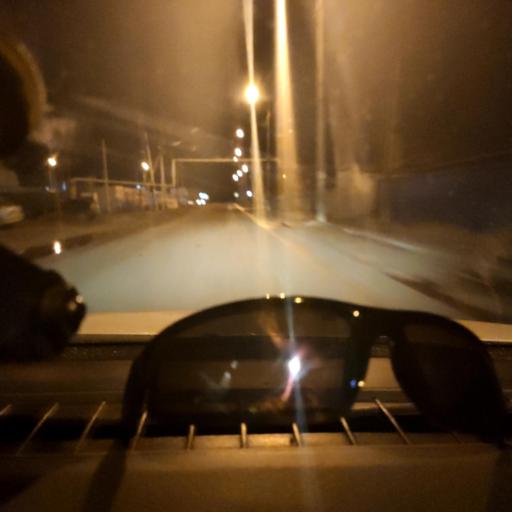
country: RU
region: Samara
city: Samara
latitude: 53.1360
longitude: 50.2357
